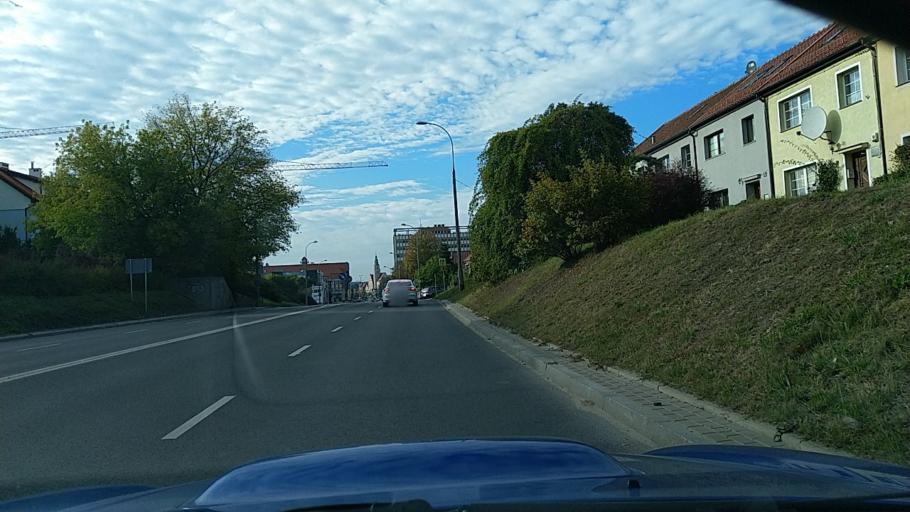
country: PL
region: Warmian-Masurian Voivodeship
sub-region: Powiat olsztynski
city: Olsztyn
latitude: 53.7750
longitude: 20.4934
